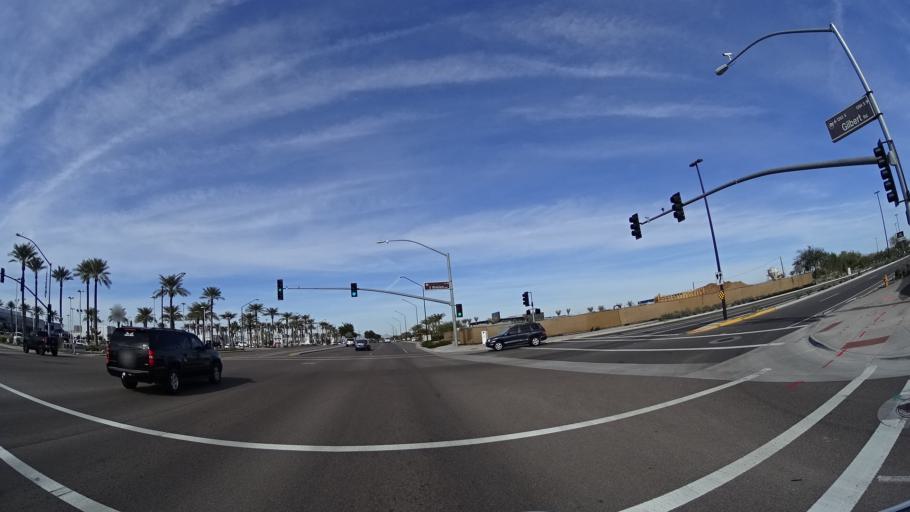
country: US
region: Arizona
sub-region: Maricopa County
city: Chandler
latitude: 33.2857
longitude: -111.7895
